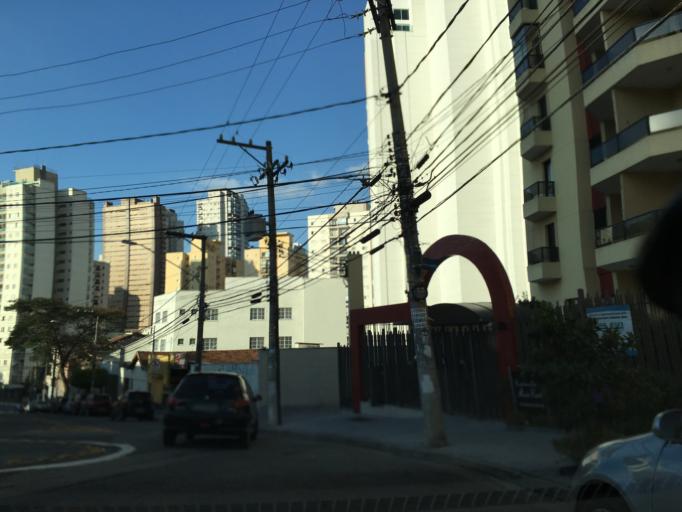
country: BR
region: Sao Paulo
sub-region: Sao Paulo
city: Sao Paulo
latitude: -23.4994
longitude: -46.6386
